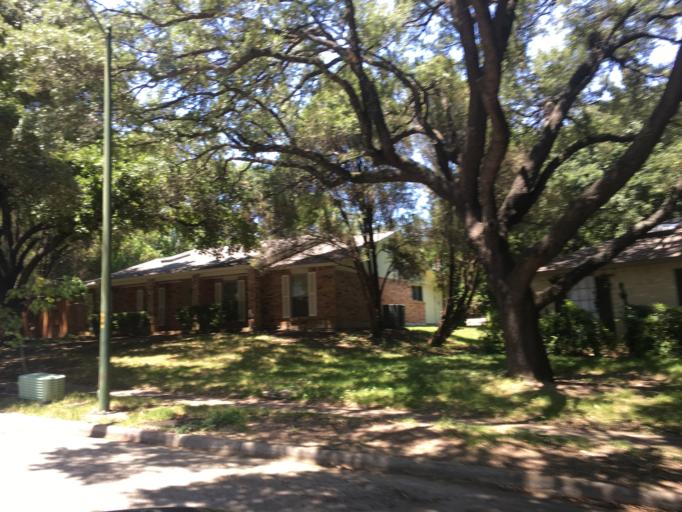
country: US
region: Texas
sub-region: Dallas County
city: Highland Park
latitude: 32.8373
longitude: -96.7334
